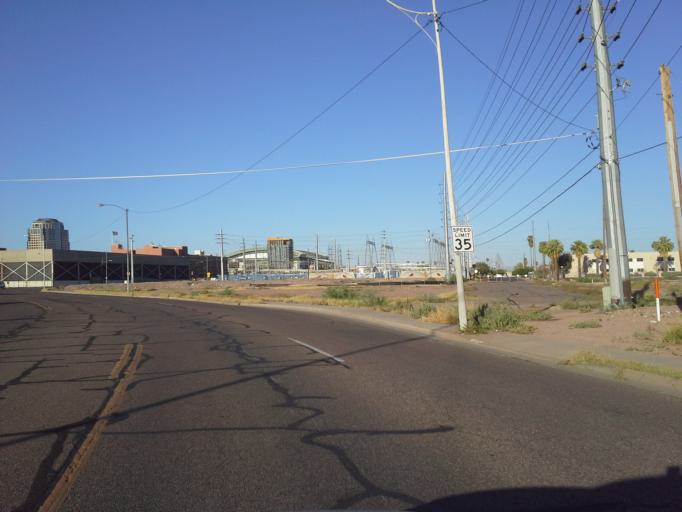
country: US
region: Arizona
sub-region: Maricopa County
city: Phoenix
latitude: 33.4411
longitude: -112.0813
